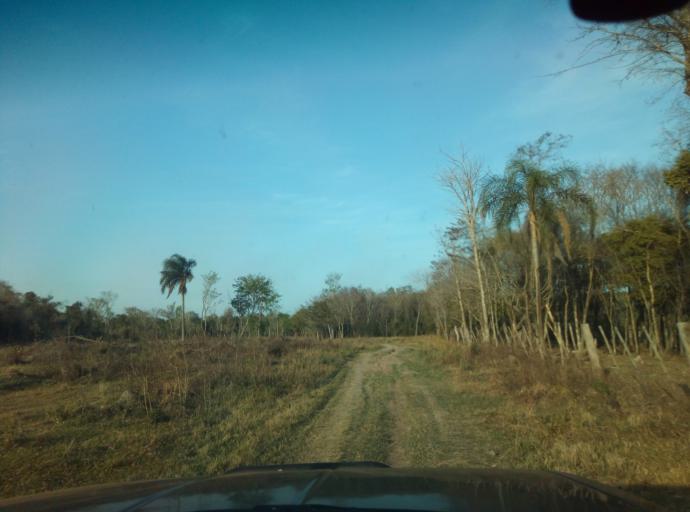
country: PY
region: Caaguazu
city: Yhu
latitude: -25.1990
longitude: -56.1130
